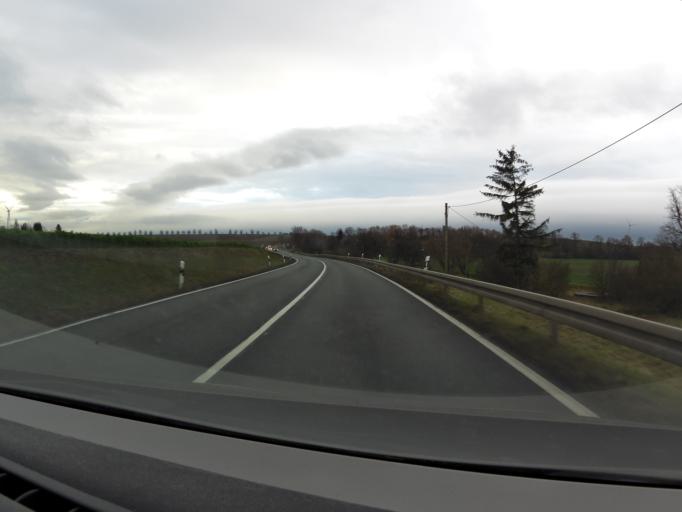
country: DE
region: Saxony-Anhalt
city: Hettstedt
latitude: 51.6851
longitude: 11.4554
